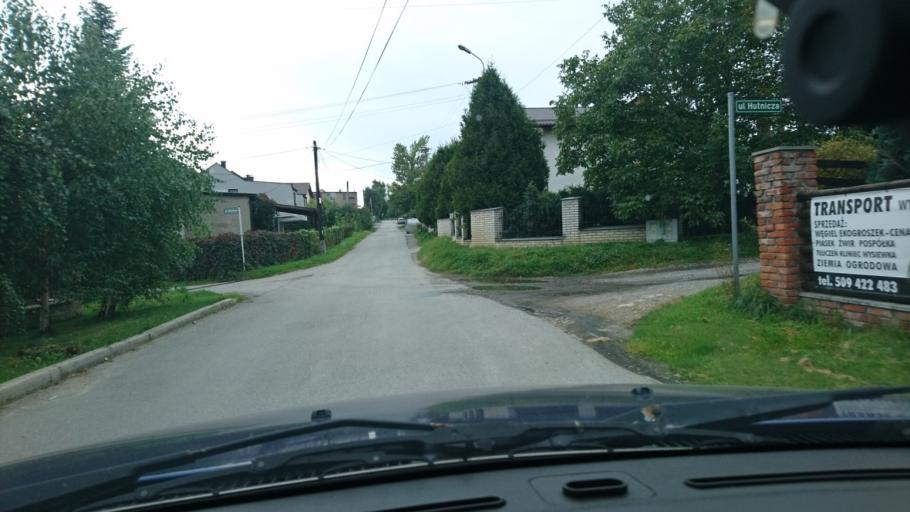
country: PL
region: Silesian Voivodeship
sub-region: Powiat bielski
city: Mazancowice
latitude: 49.8245
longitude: 18.9996
